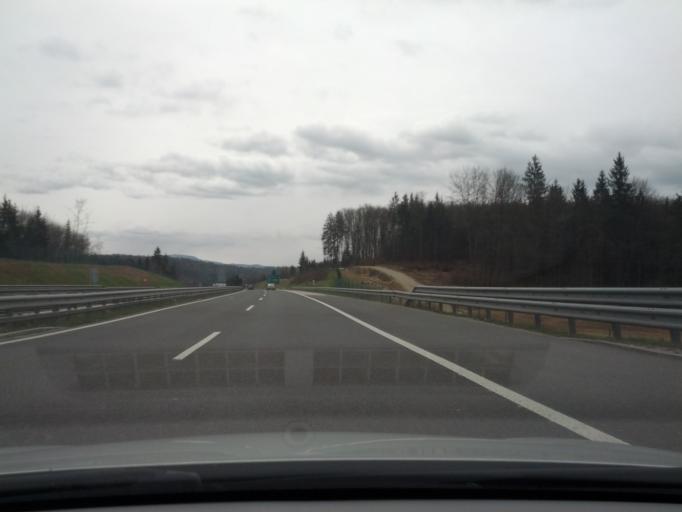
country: SI
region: Mirna Pec
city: Mirna Pec
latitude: 45.8792
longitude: 15.0810
